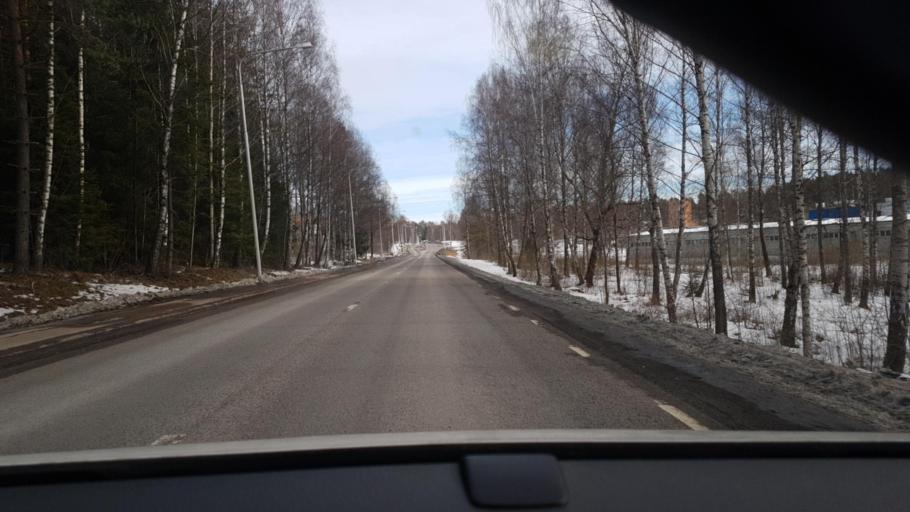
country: SE
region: Vaermland
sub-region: Arvika Kommun
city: Arvika
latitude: 59.6713
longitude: 12.4853
